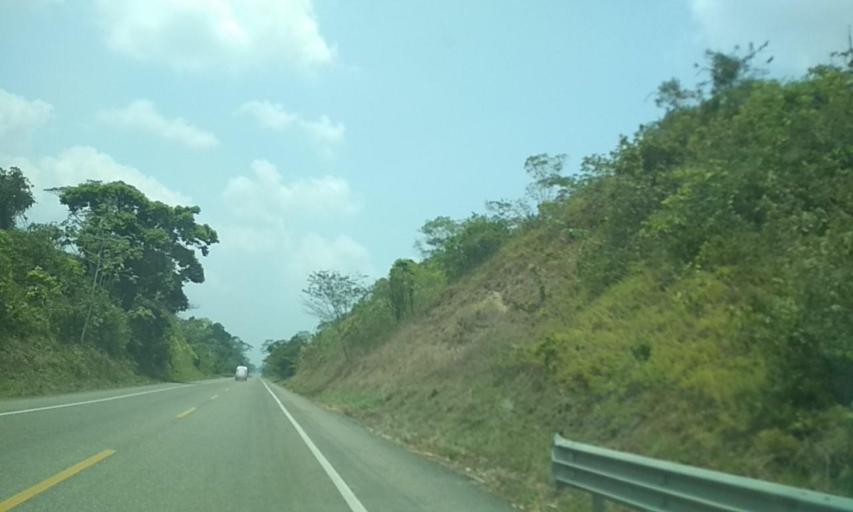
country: MX
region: Tabasco
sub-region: Huimanguillo
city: Francisco Rueda
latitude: 17.6629
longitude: -93.8574
